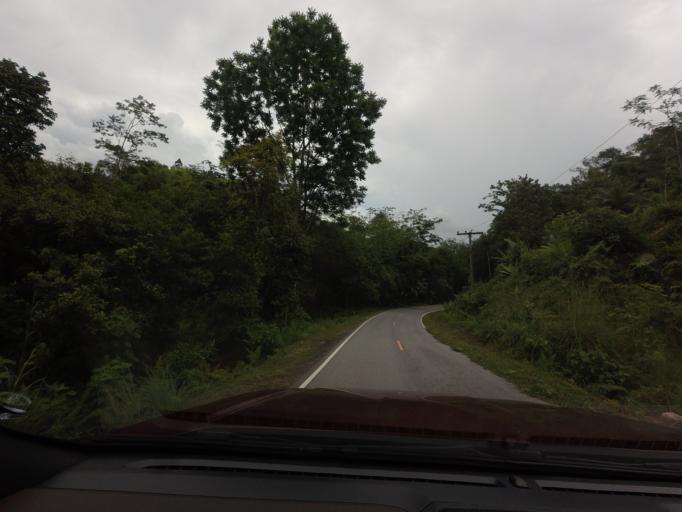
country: TH
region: Narathiwat
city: Sukhirin
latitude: 5.9830
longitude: 101.6821
